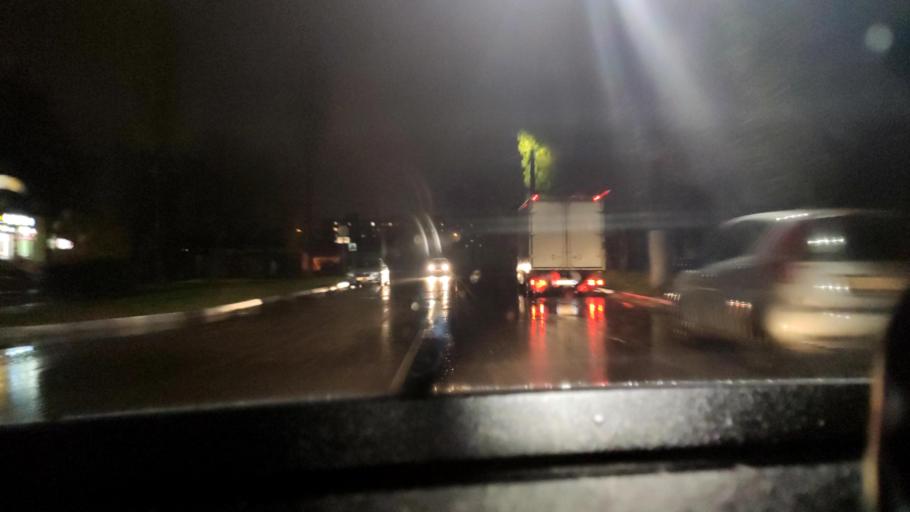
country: RU
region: Voronezj
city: Pridonskoy
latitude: 51.6559
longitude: 39.1178
